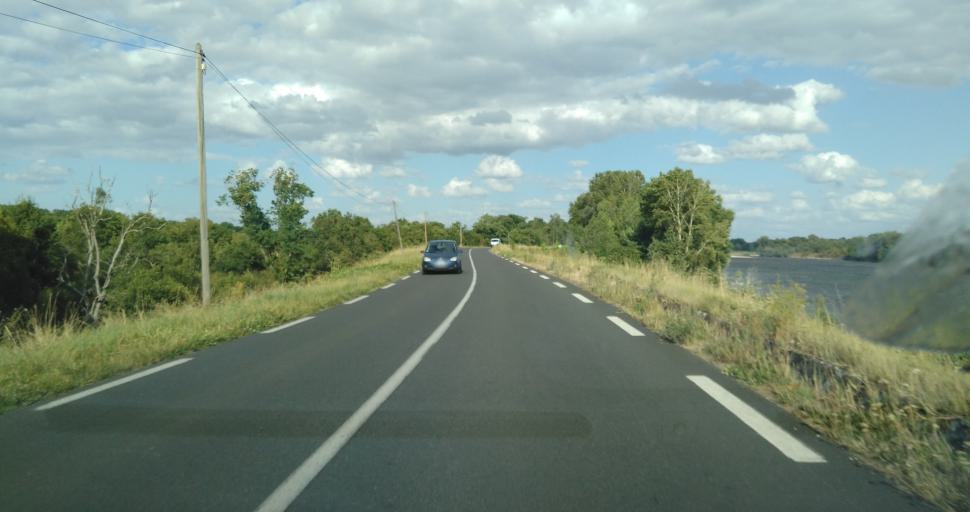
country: FR
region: Centre
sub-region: Departement d'Indre-et-Loire
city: Saint-Etienne-de-Chigny
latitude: 47.3693
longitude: 0.5291
